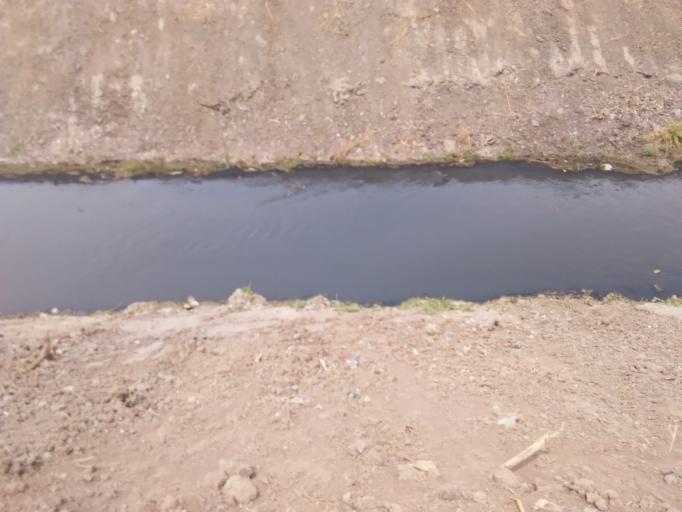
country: MX
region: Nayarit
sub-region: Tepic
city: La Corregidora
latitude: 21.4835
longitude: -104.8459
